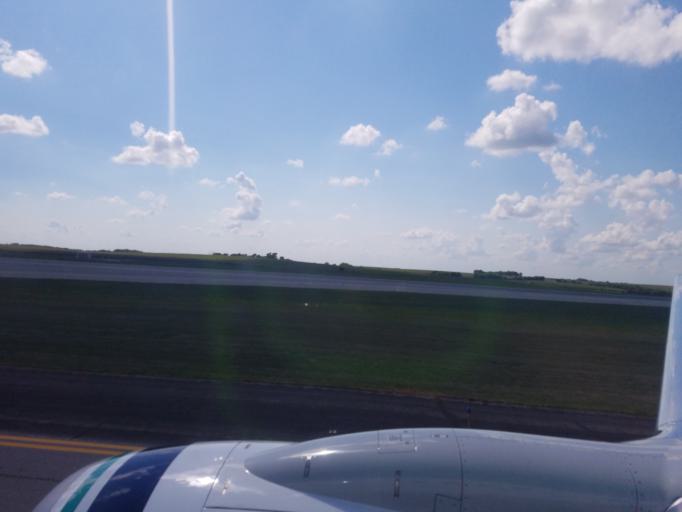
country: US
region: Missouri
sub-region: Platte County
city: Weatherby Lake
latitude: 39.3093
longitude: -94.7229
